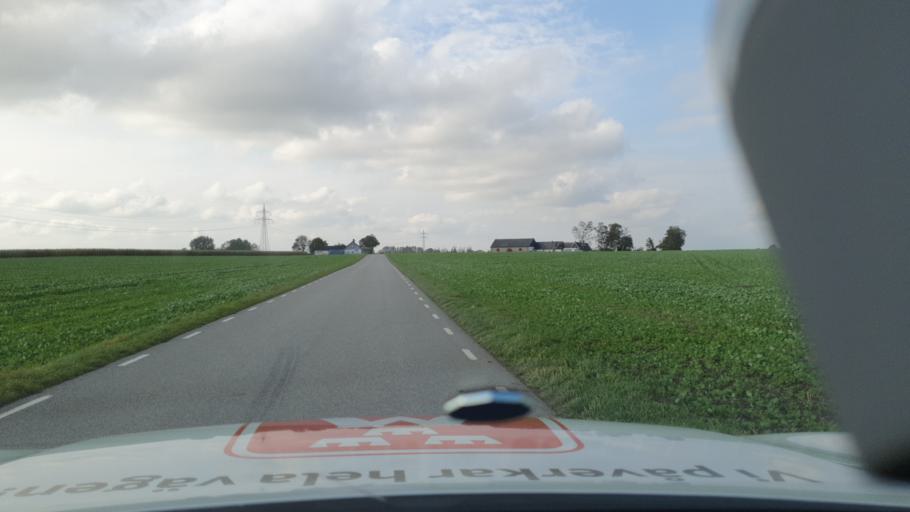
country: SE
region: Skane
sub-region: Malmo
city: Oxie
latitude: 55.4899
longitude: 13.0767
